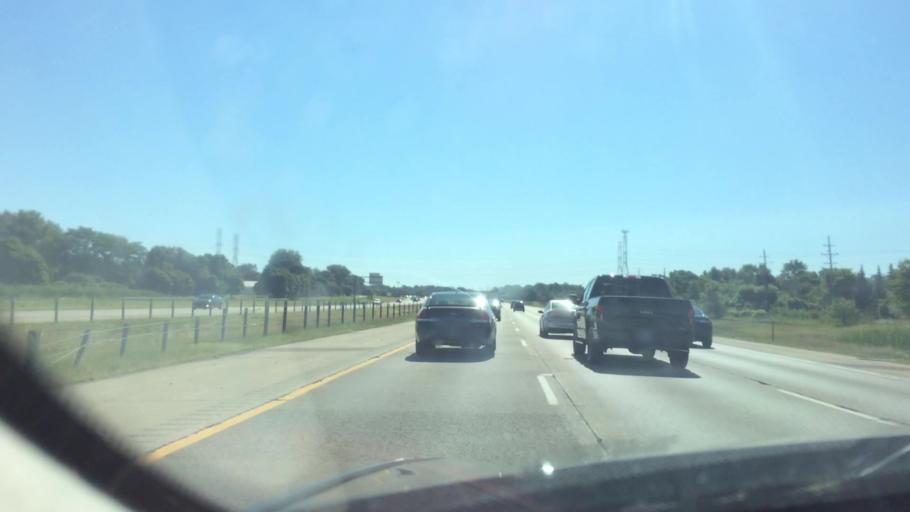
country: US
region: Michigan
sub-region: Wayne County
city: Belleville
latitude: 42.2199
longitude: -83.4619
